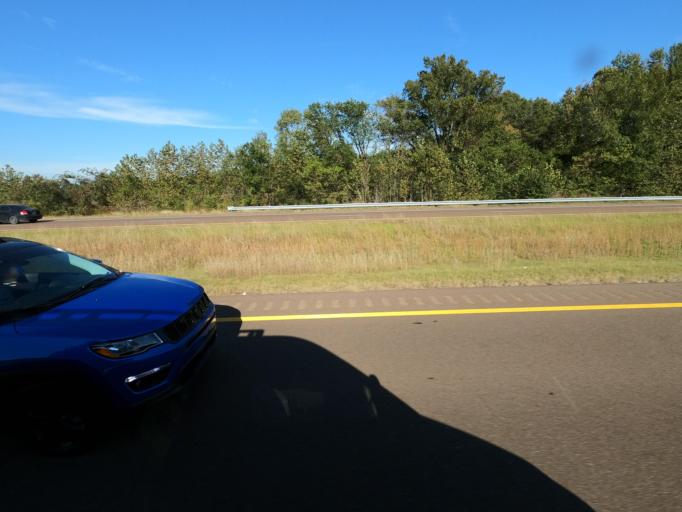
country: US
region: Tennessee
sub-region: Lauderdale County
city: Halls
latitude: 35.9289
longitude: -89.2850
